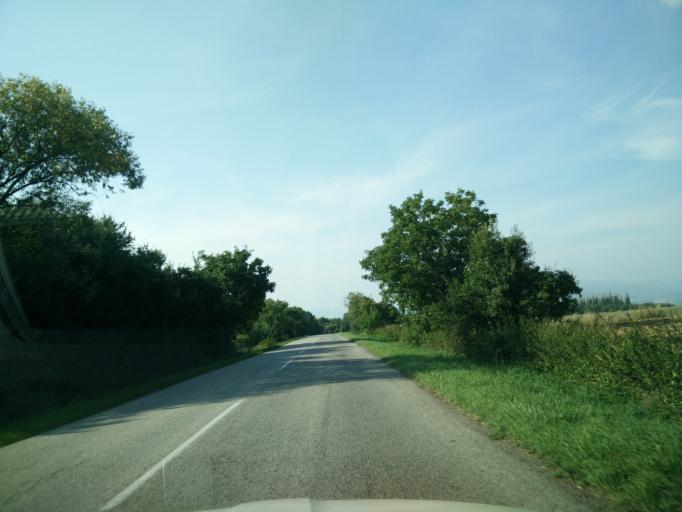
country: SK
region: Nitriansky
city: Novaky
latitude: 48.7024
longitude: 18.5918
